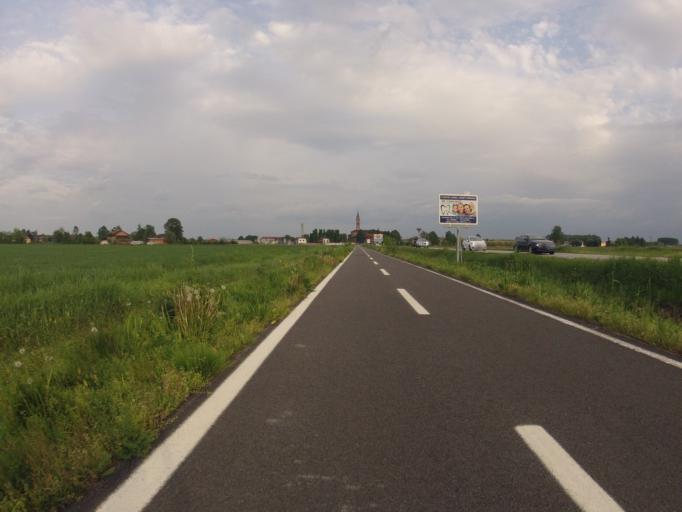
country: IT
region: Piedmont
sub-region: Provincia di Cuneo
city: Moretta
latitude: 44.7710
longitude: 7.5254
